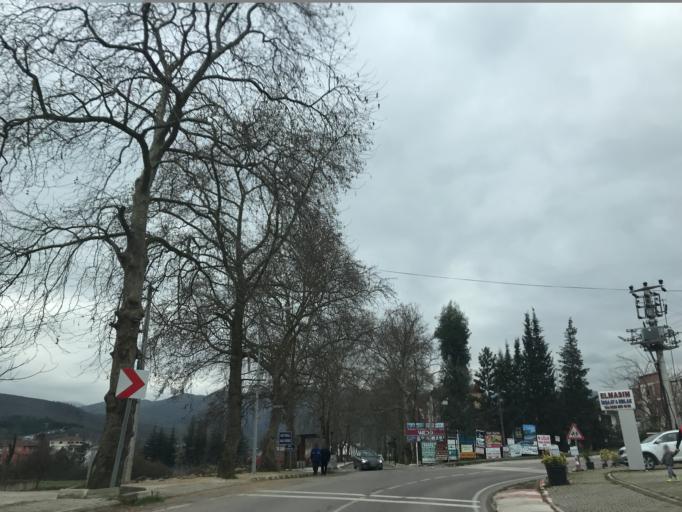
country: TR
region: Yalova
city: Kadikoy
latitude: 40.6111
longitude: 29.2110
